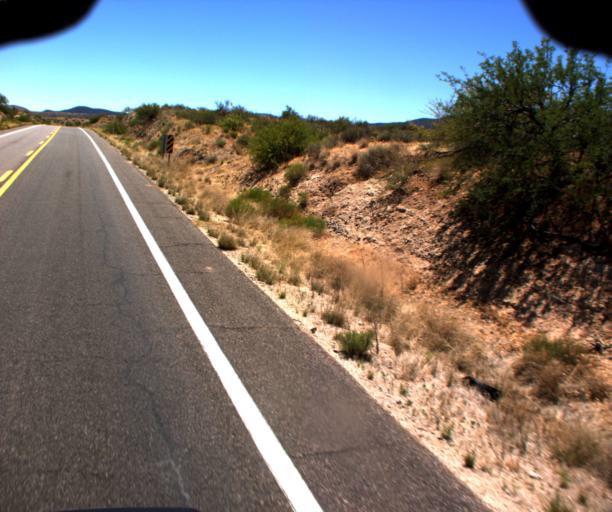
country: US
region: Arizona
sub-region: Gila County
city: Globe
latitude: 33.3584
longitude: -110.7356
